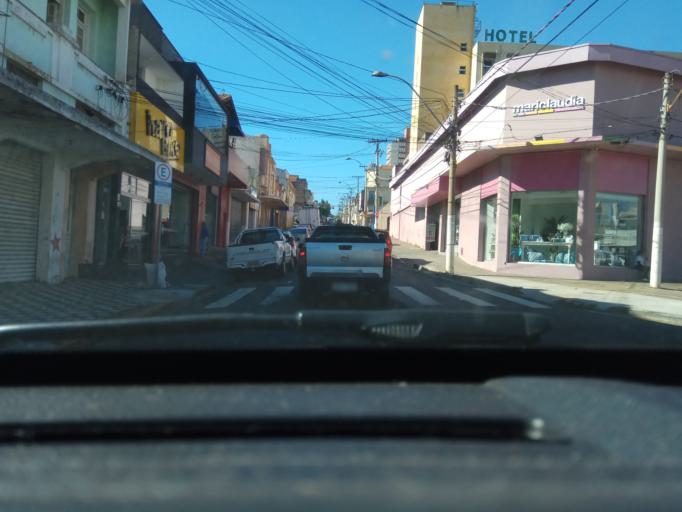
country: BR
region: Sao Paulo
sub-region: Piracicaba
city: Piracicaba
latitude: -22.7264
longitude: -47.6465
